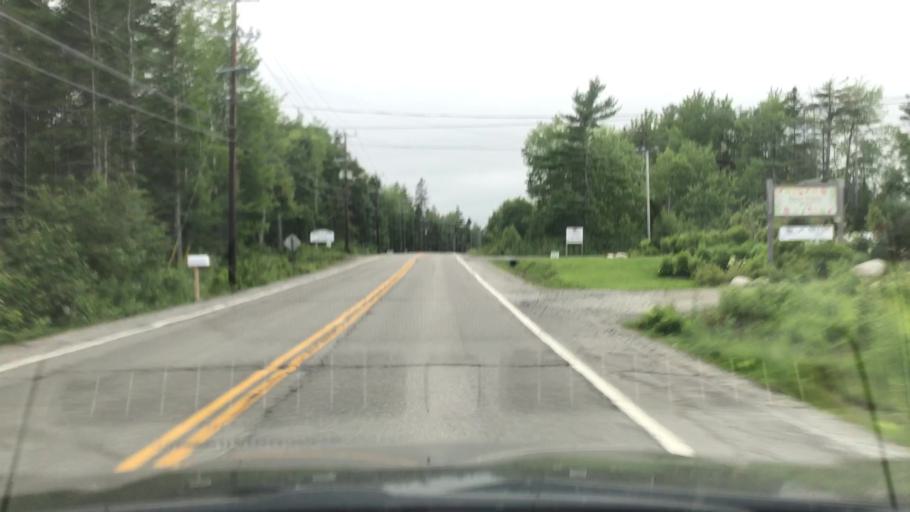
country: US
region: Maine
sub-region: Hancock County
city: Trenton
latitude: 44.4078
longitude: -68.3500
